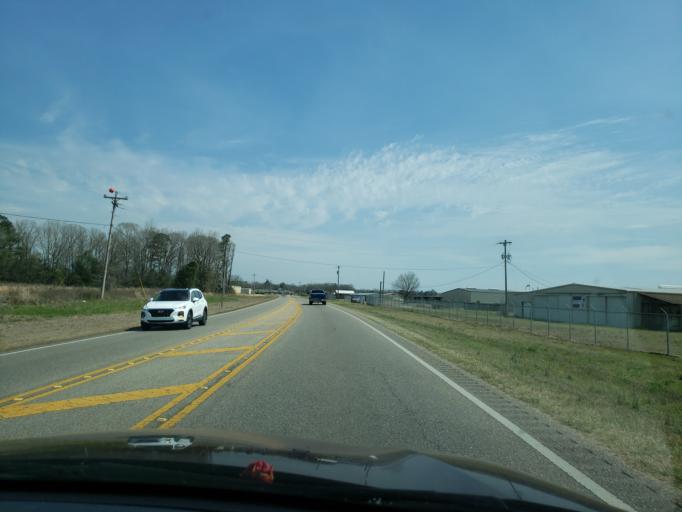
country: US
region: Alabama
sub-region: Elmore County
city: Elmore
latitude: 32.5311
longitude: -86.3335
